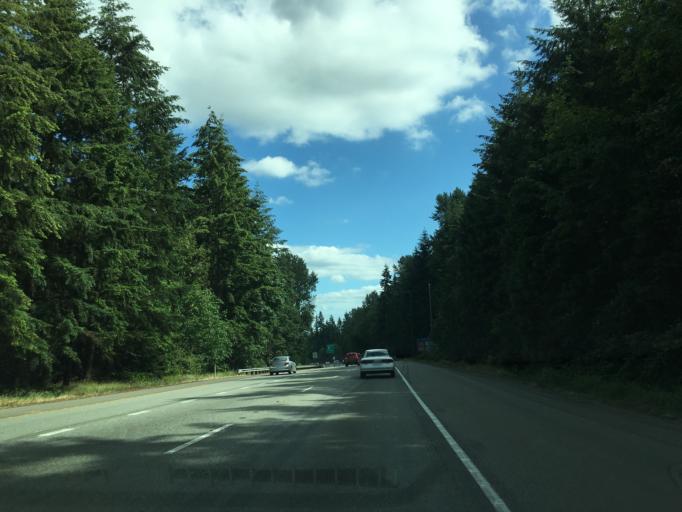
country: US
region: Washington
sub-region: King County
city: Bothell
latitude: 47.8026
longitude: -122.2260
